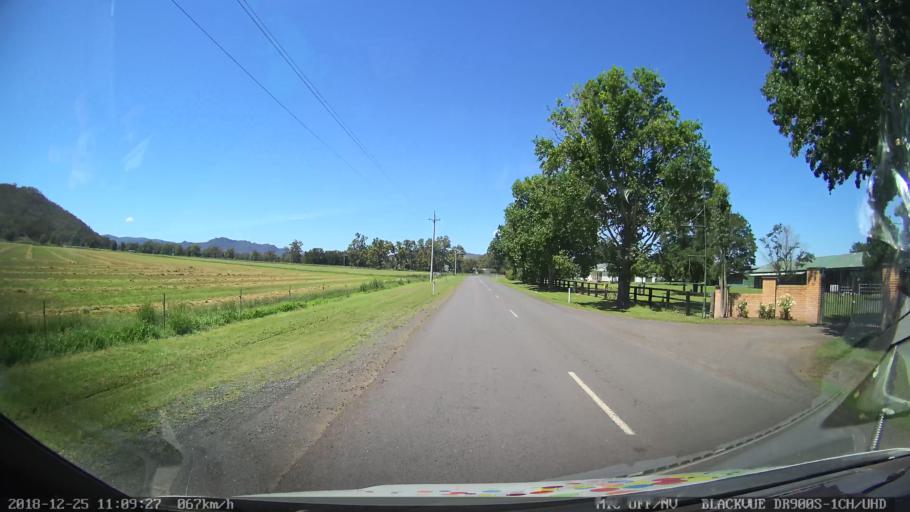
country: AU
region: New South Wales
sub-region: Upper Hunter Shire
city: Merriwa
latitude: -32.4113
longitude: 150.1186
